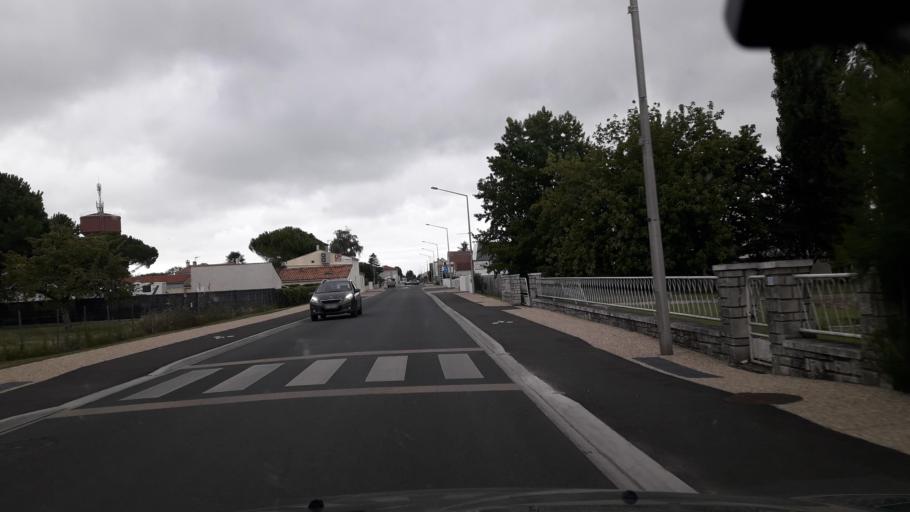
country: FR
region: Poitou-Charentes
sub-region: Departement de la Charente-Maritime
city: Arvert
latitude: 45.7416
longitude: -1.1197
